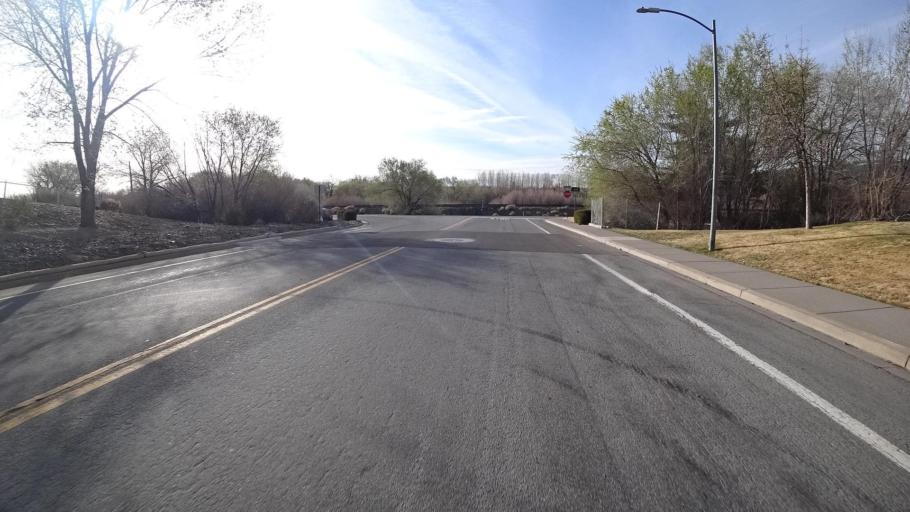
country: US
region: Nevada
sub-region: Washoe County
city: Reno
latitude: 39.5199
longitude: -119.8480
